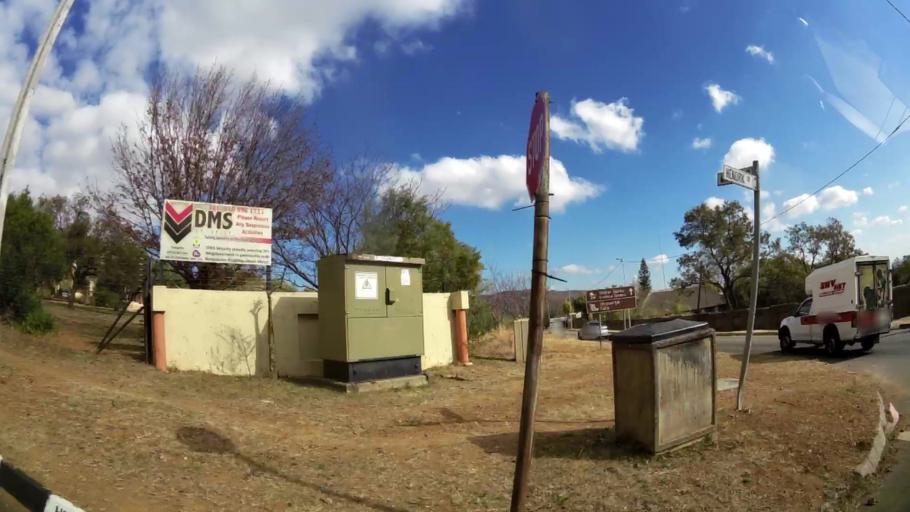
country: ZA
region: Gauteng
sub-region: West Rand District Municipality
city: Muldersdriseloop
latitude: -26.0904
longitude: 27.8527
